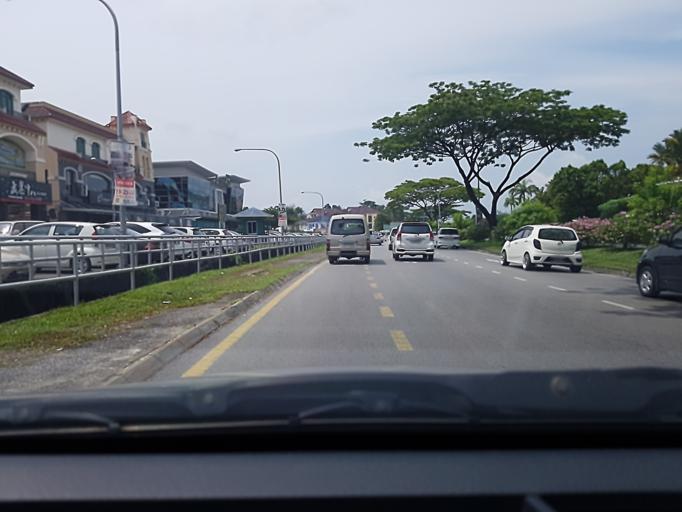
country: MY
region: Sarawak
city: Kuching
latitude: 1.5173
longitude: 110.3661
